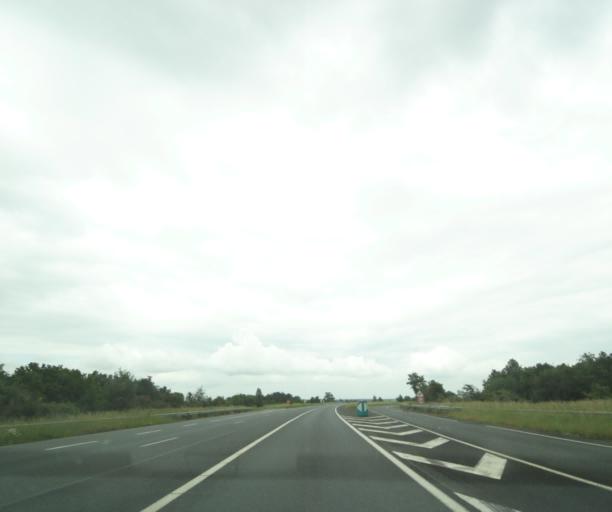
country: FR
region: Poitou-Charentes
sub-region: Departement des Deux-Sevres
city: Saint-Varent
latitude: 46.8665
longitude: -0.2055
